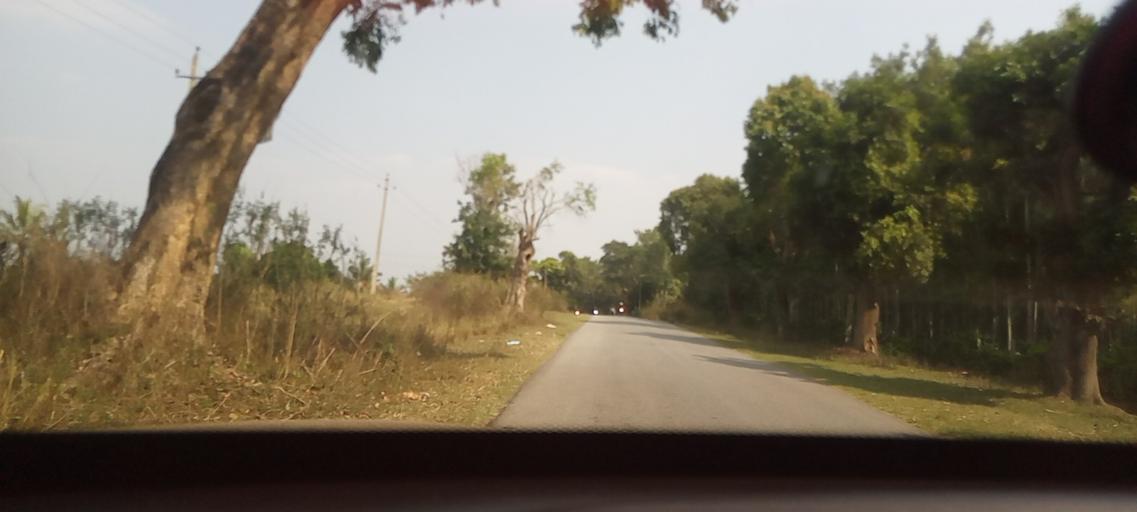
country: IN
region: Karnataka
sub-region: Hassan
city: Belur
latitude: 13.1825
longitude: 75.8388
